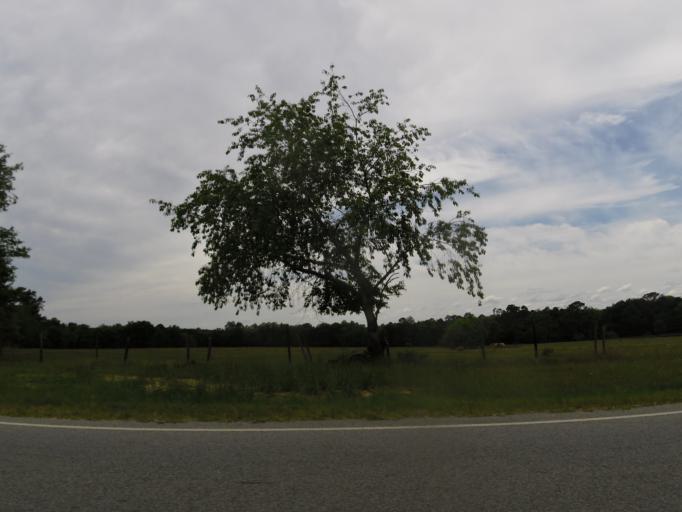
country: US
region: Georgia
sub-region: Emanuel County
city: Twin City
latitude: 32.4823
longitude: -82.2446
